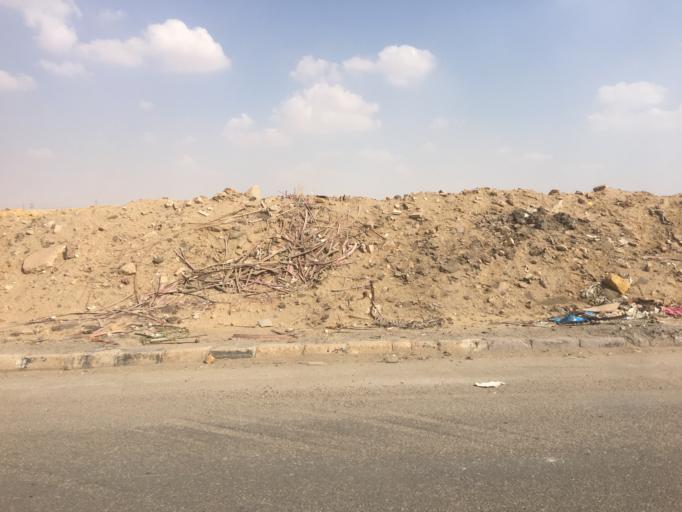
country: EG
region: Eastern Province
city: Bilbays
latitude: 30.2584
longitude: 31.7666
